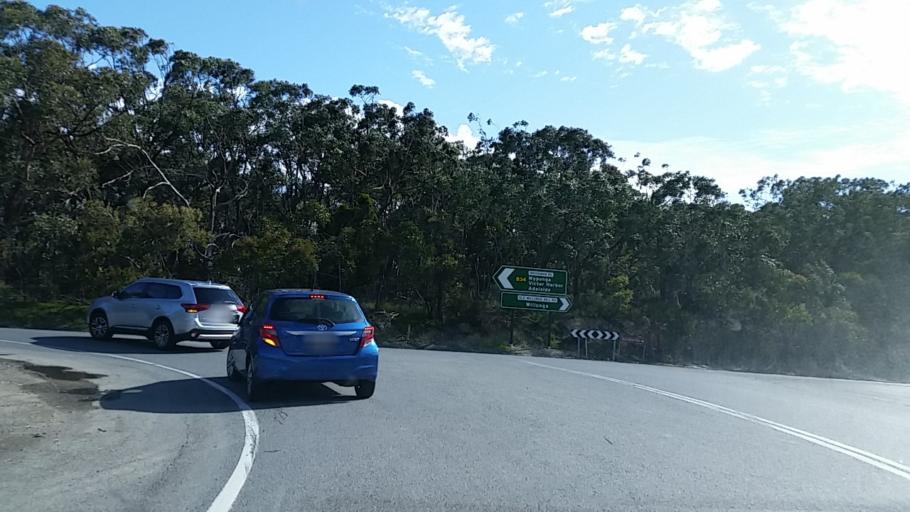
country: AU
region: South Australia
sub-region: Alexandrina
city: Mount Compass
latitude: -35.2917
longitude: 138.5802
